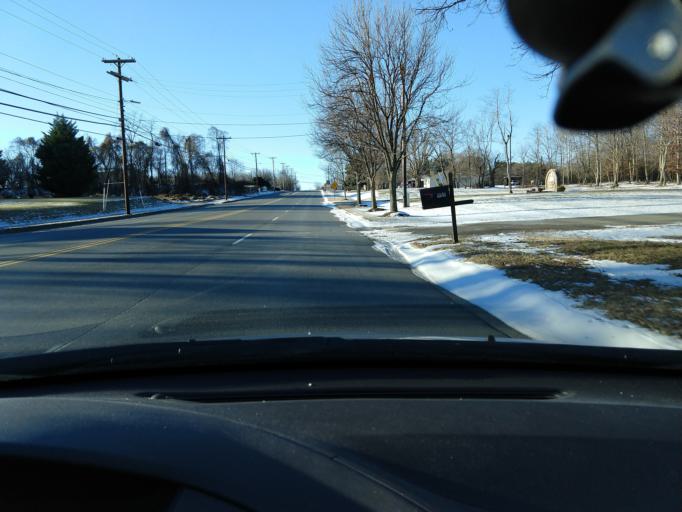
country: US
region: Virginia
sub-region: City of Bedford
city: Bedford
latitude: 37.3191
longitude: -79.5355
